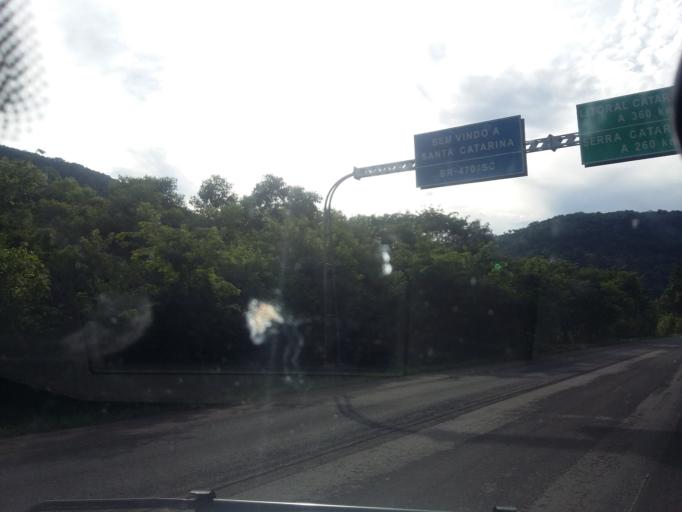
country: BR
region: Santa Catarina
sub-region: Celso Ramos
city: Celso Ramos
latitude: -27.5995
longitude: -51.4727
